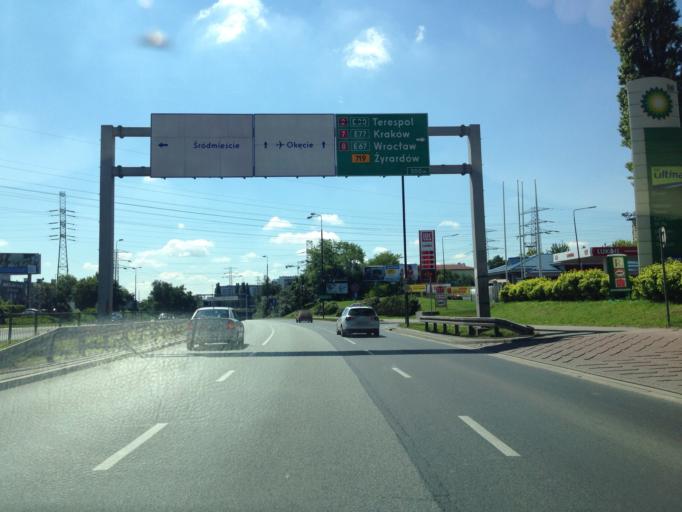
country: PL
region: Masovian Voivodeship
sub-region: Warszawa
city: Ochota
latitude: 52.2228
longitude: 20.9583
